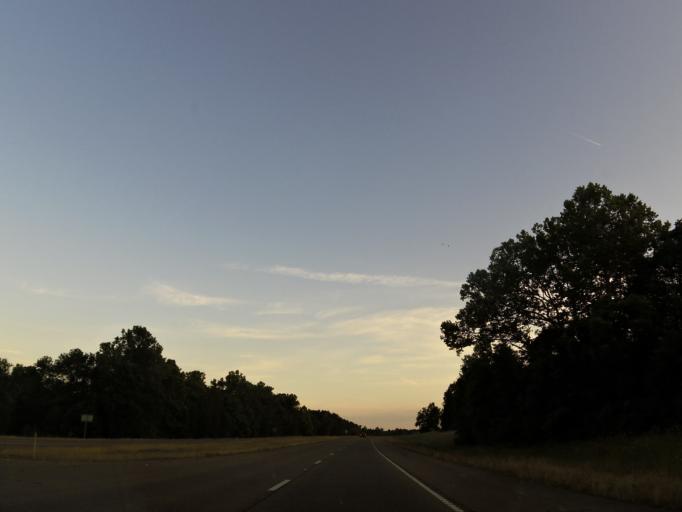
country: US
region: Mississippi
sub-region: Noxubee County
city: Macon
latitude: 33.1004
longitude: -88.5473
